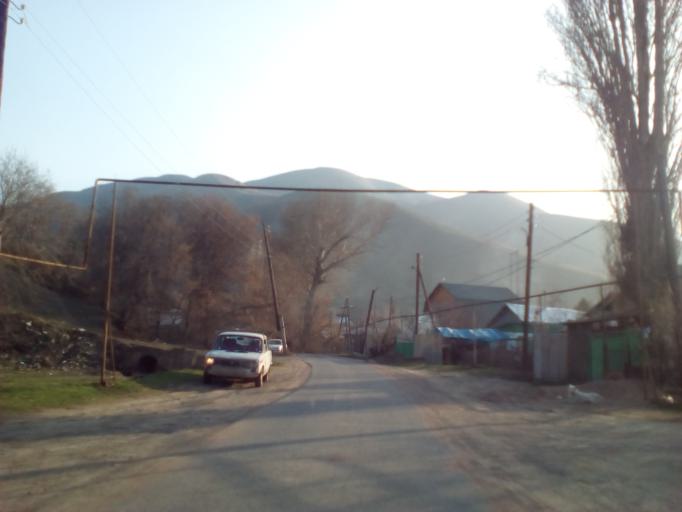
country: KZ
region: Almaty Oblysy
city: Burunday
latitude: 43.1535
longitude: 76.4266
